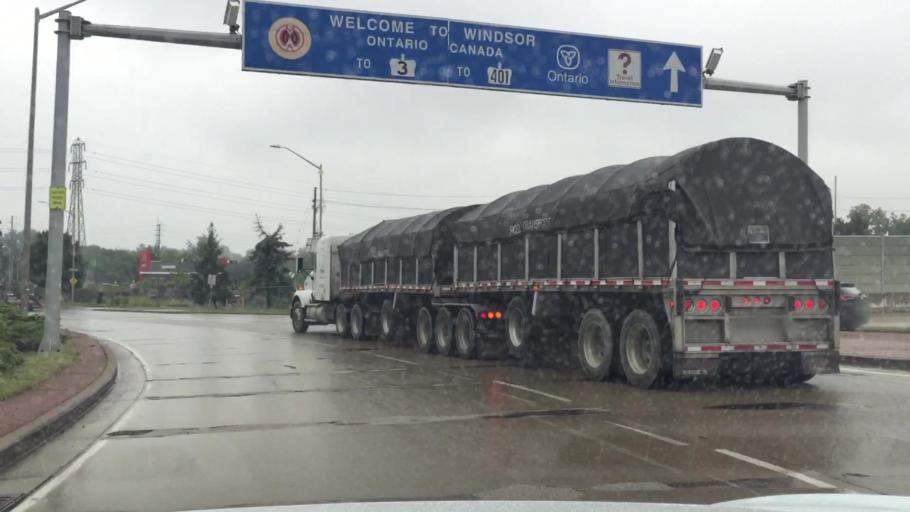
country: US
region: Michigan
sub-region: Wayne County
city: Detroit
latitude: 42.3004
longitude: -83.0660
